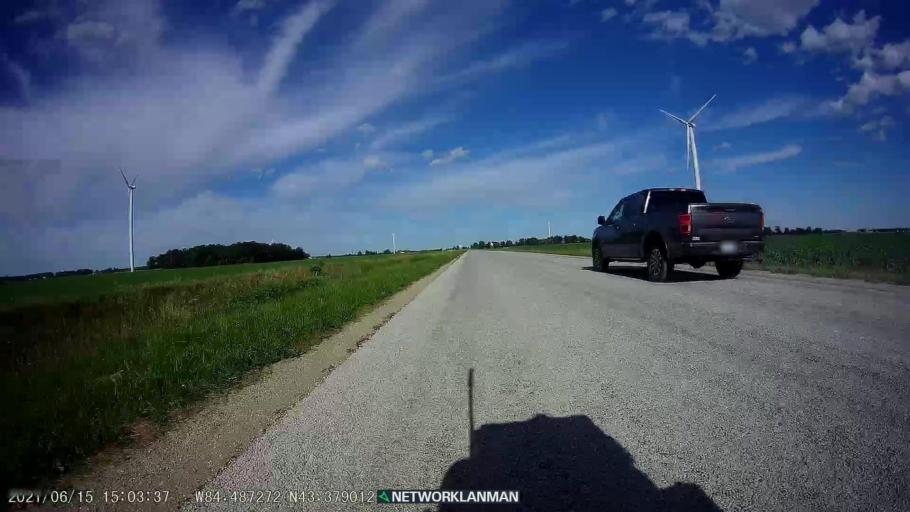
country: US
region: Michigan
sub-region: Gratiot County
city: Breckenridge
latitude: 43.3791
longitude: -84.4875
